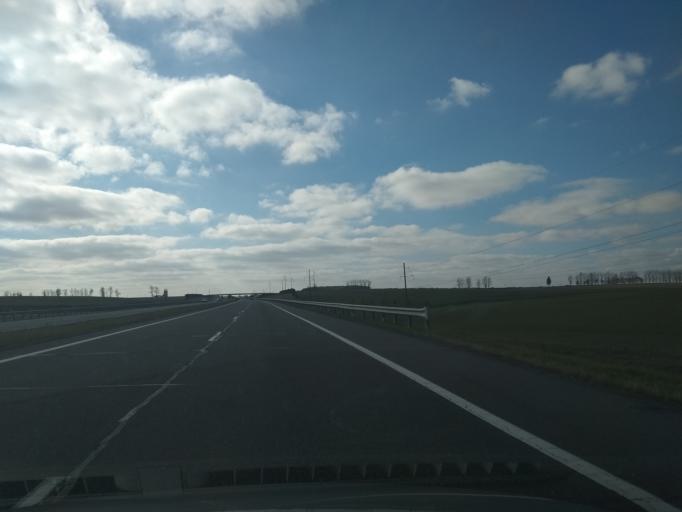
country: BY
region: Minsk
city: Novy Svyerzhan'
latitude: 53.4854
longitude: 26.6332
